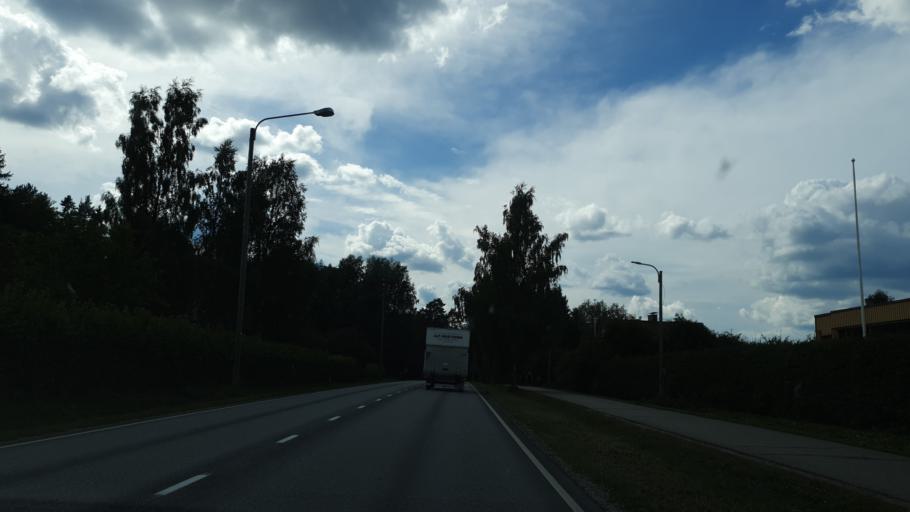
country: FI
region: Kainuu
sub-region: Kajaani
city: Sotkamo
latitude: 64.1333
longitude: 28.4062
